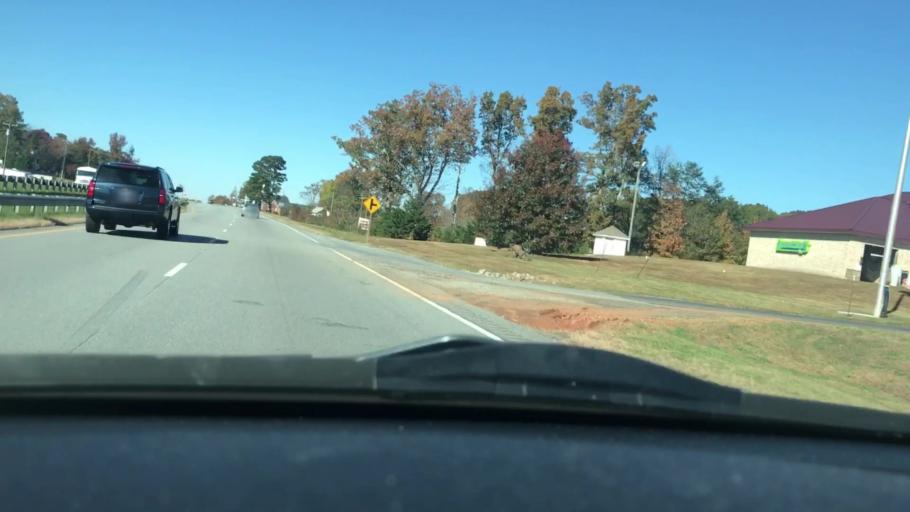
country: US
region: North Carolina
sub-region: Rockingham County
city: Madison
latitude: 36.3110
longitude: -79.9418
